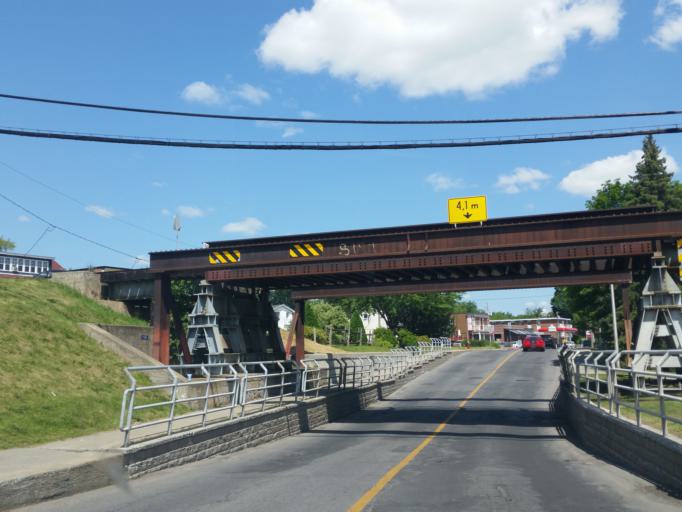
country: CA
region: Quebec
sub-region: Monteregie
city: Saint-Jean-sur-Richelieu
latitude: 45.3096
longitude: -73.2515
